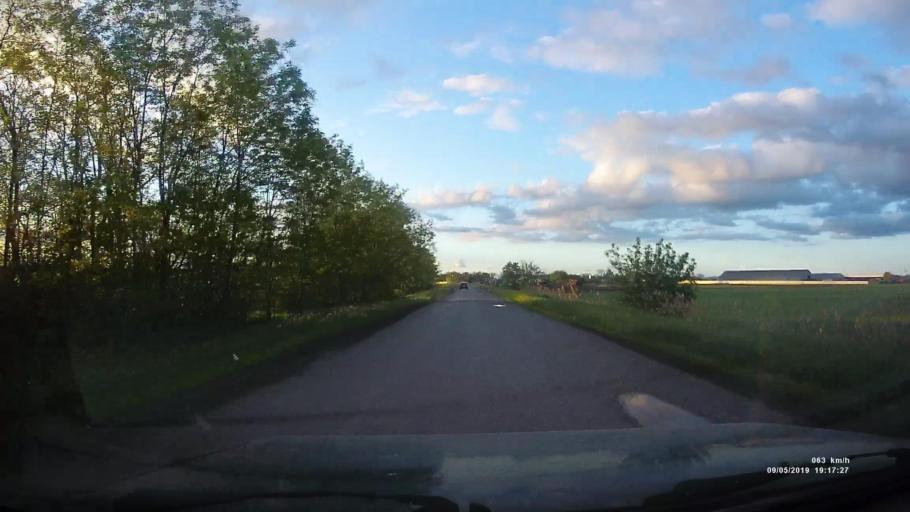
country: RU
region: Krasnodarskiy
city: Kanelovskaya
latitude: 46.7856
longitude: 39.2118
